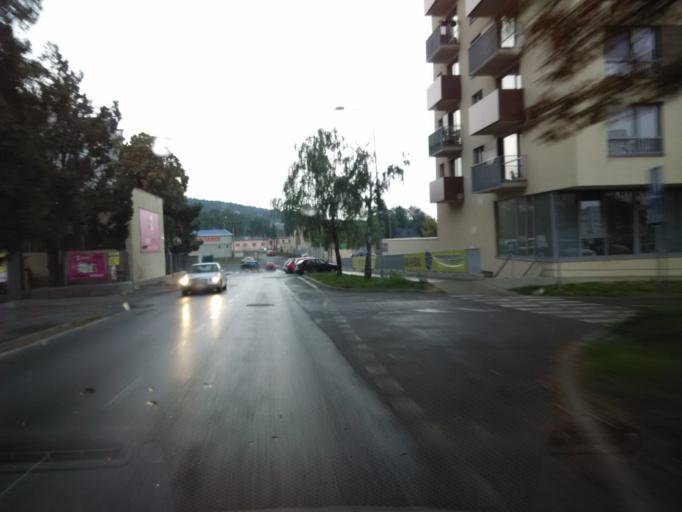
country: SK
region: Nitriansky
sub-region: Okres Nitra
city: Nitra
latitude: 48.2994
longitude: 18.0821
